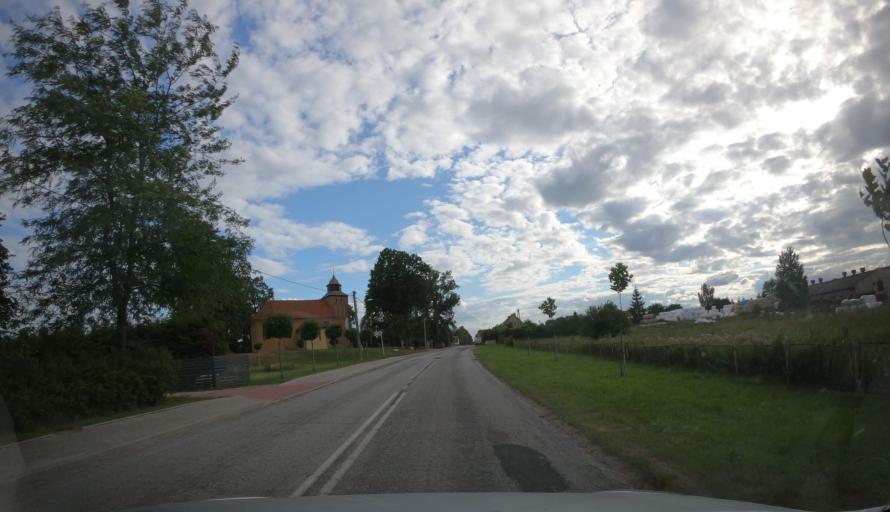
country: PL
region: West Pomeranian Voivodeship
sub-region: Powiat slawienski
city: Slawno
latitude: 54.3257
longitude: 16.6909
